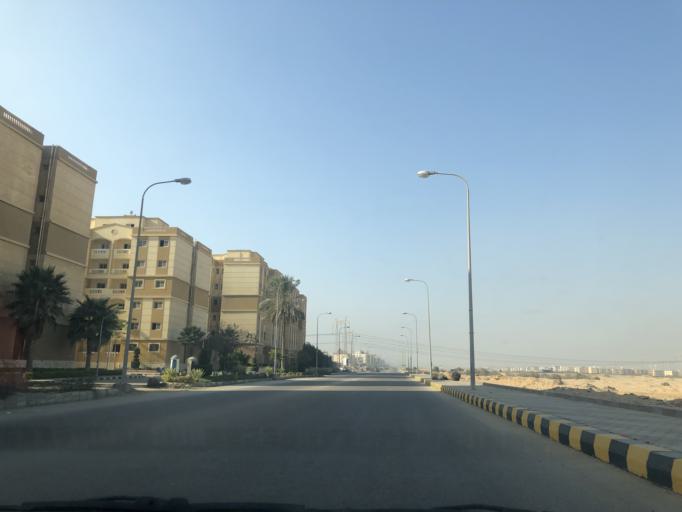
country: EG
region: Al Jizah
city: Madinat Sittah Uktubar
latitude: 29.9200
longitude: 31.0566
